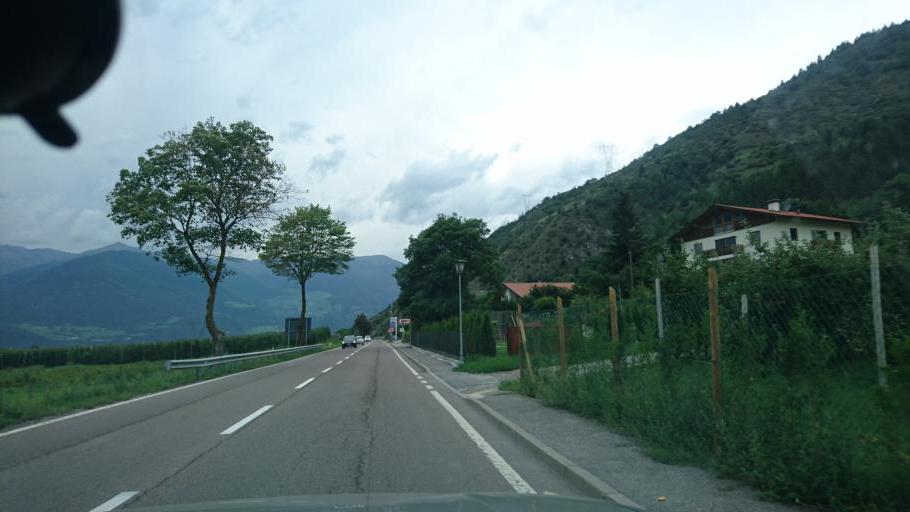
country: IT
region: Trentino-Alto Adige
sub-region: Bolzano
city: Prato Allo Stelvio
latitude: 46.6303
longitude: 10.6394
